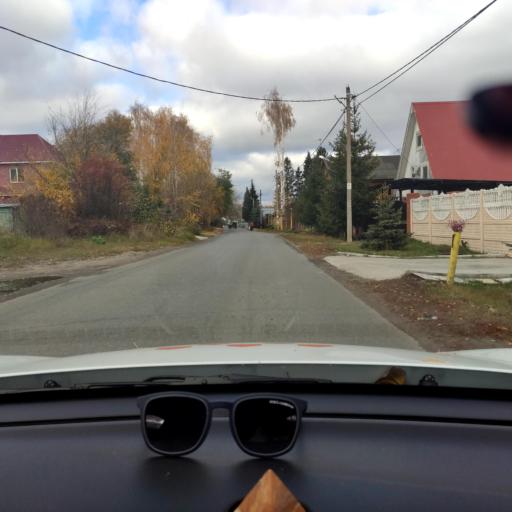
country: RU
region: Tatarstan
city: Verkhniy Uslon
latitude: 55.6192
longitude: 49.0145
